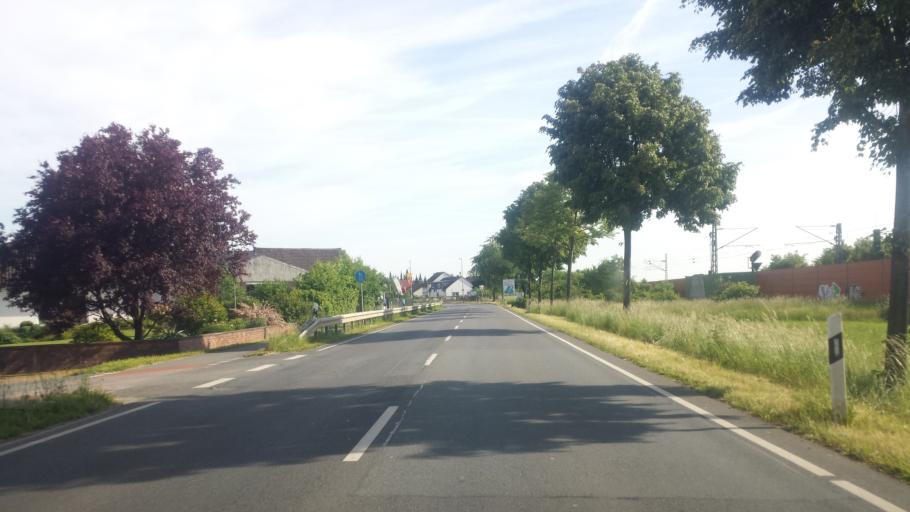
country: DE
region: Hesse
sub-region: Regierungsbezirk Darmstadt
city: Gross-Rohrheim
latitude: 49.7315
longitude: 8.4897
